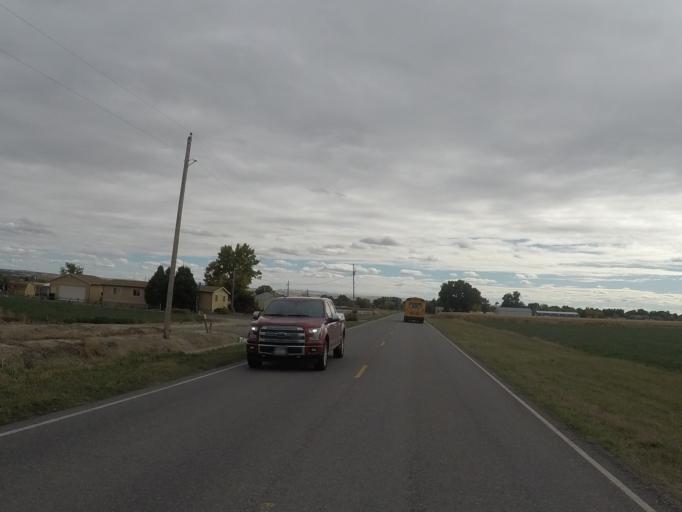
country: US
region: Montana
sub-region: Yellowstone County
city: Laurel
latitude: 45.7457
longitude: -108.6588
